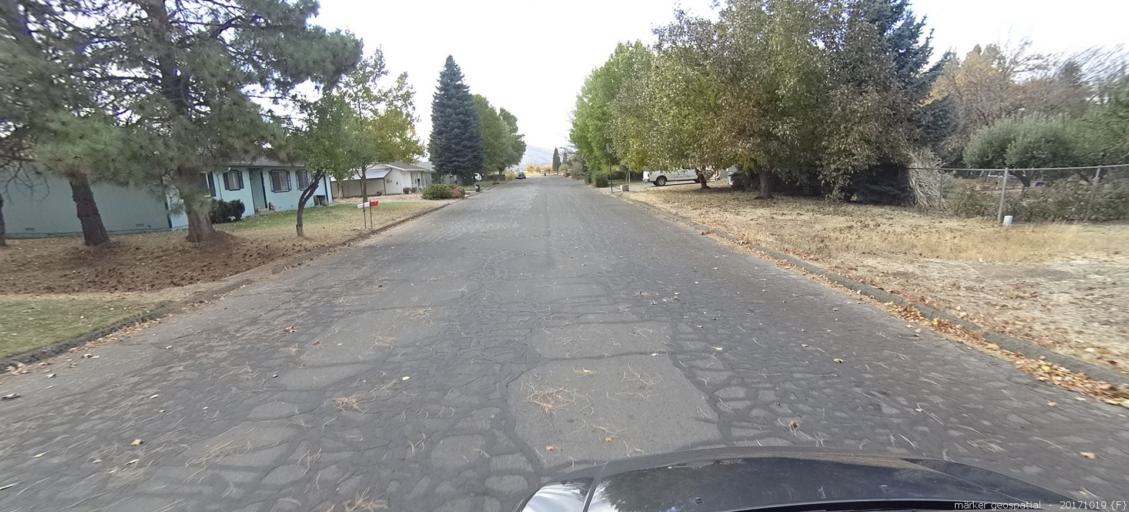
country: US
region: California
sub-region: Shasta County
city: Burney
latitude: 41.0277
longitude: -121.4257
